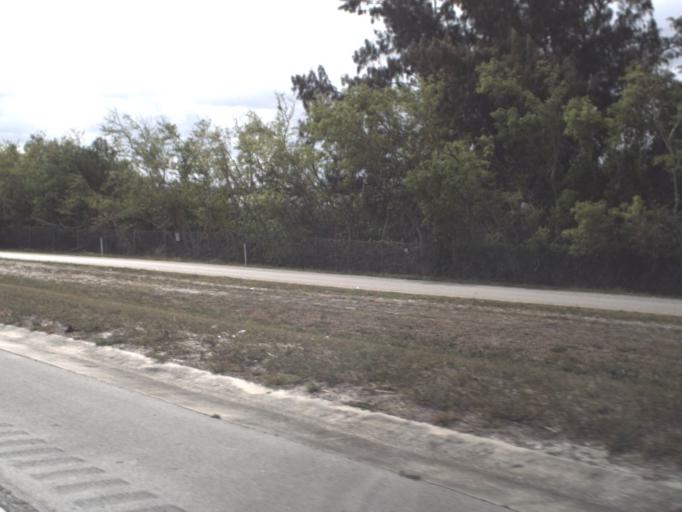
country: US
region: Florida
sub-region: Brevard County
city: South Patrick Shores
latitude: 28.2079
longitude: -80.6399
